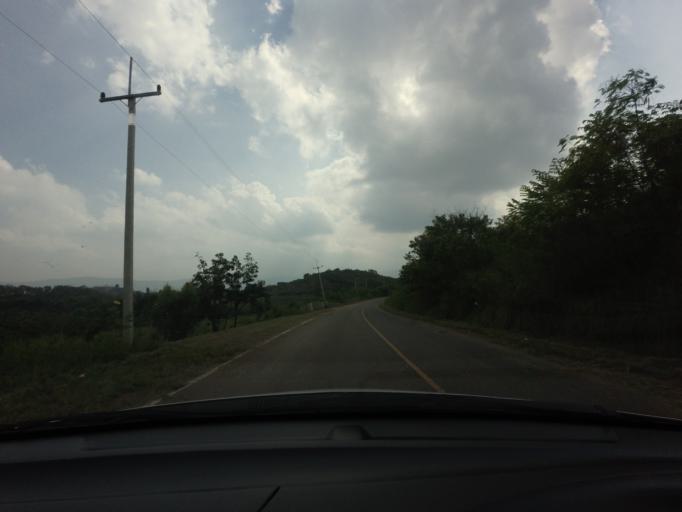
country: TH
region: Nakhon Ratchasima
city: Pak Chong
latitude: 14.5161
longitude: 101.5729
